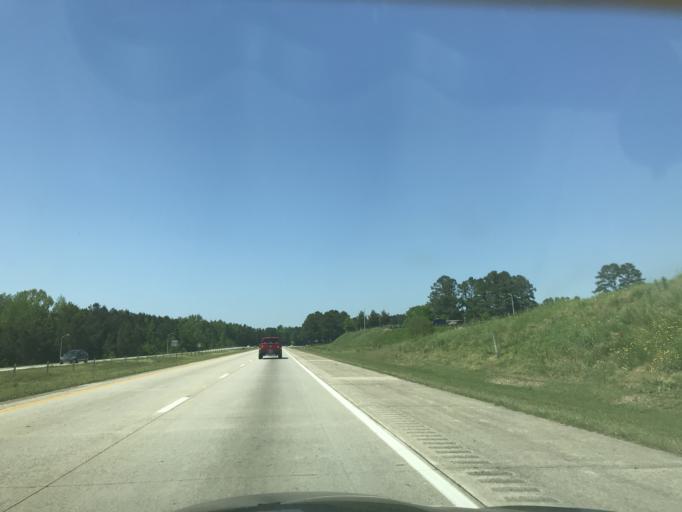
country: US
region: North Carolina
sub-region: Johnston County
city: Benson
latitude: 35.4367
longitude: -78.5335
